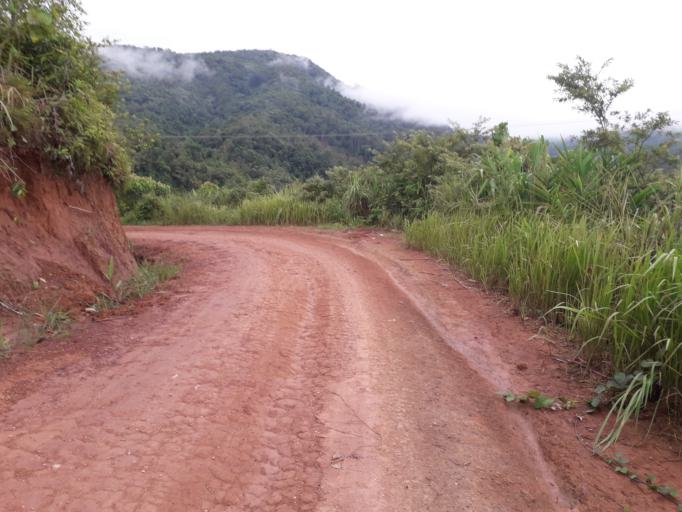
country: CN
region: Yunnan
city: Menglie
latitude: 22.2652
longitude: 101.5783
